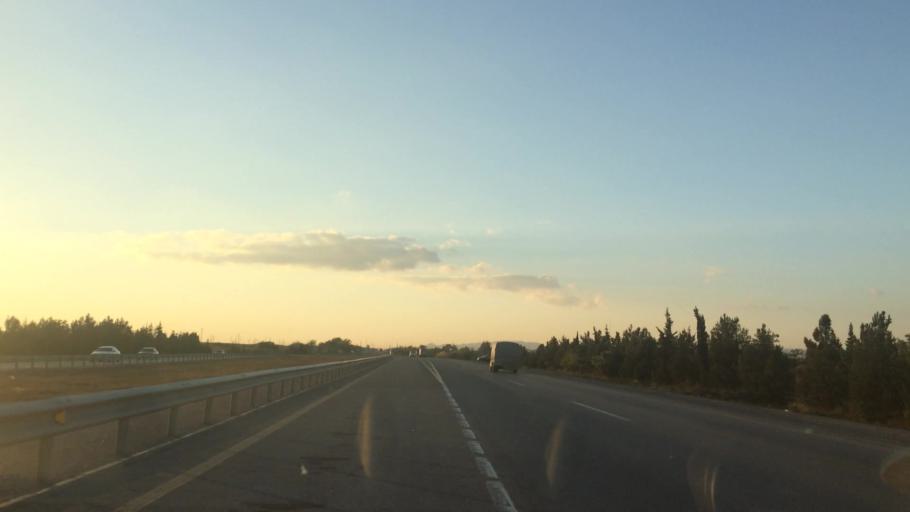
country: AZ
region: Haciqabul
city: Haciqabul
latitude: 40.0253
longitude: 49.1124
